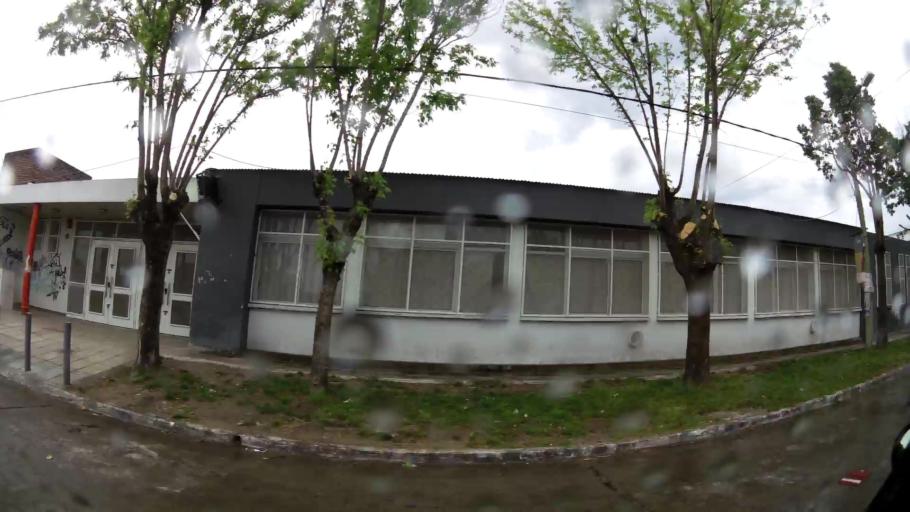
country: AR
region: Buenos Aires
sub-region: Partido de Quilmes
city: Quilmes
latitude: -34.7662
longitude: -58.2308
